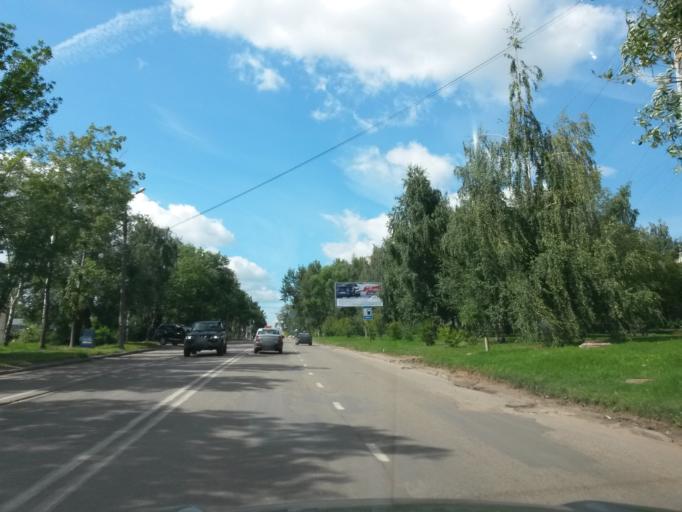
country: RU
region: Jaroslavl
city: Yaroslavl
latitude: 57.5726
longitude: 39.8531
